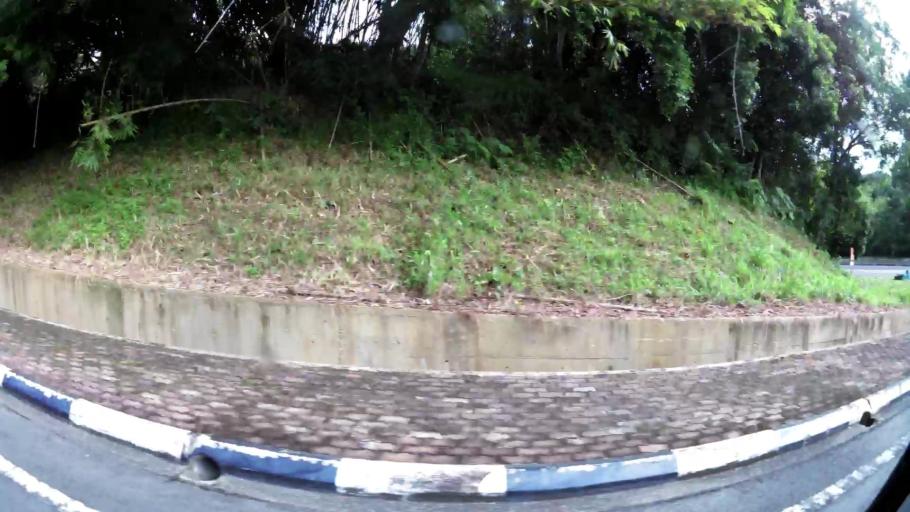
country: BN
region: Brunei and Muara
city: Bandar Seri Begawan
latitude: 4.8854
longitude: 114.9523
